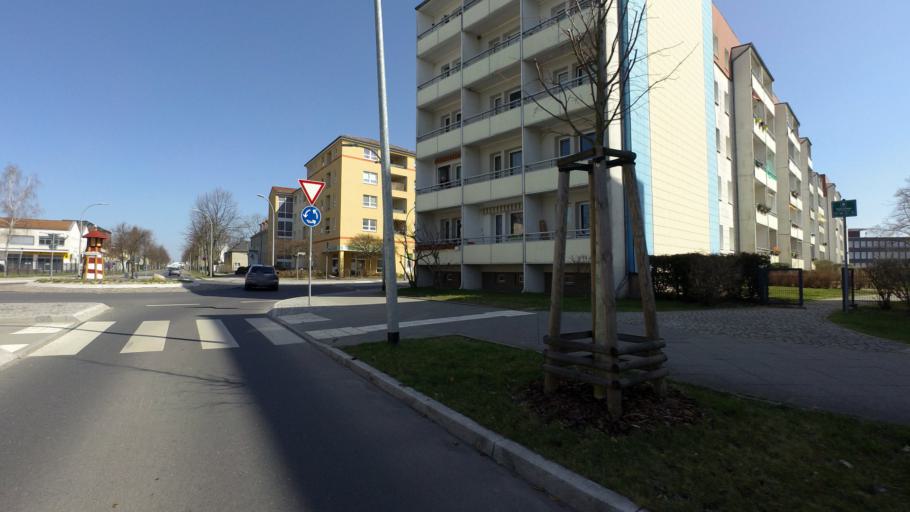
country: DE
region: Brandenburg
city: Oranienburg
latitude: 52.7580
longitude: 13.2411
